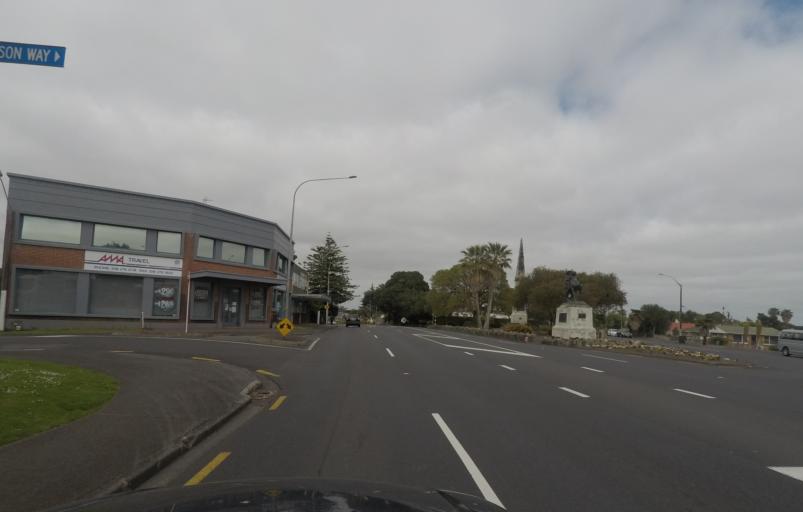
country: NZ
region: Auckland
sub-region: Auckland
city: Mangere
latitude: -36.9496
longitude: 174.8453
